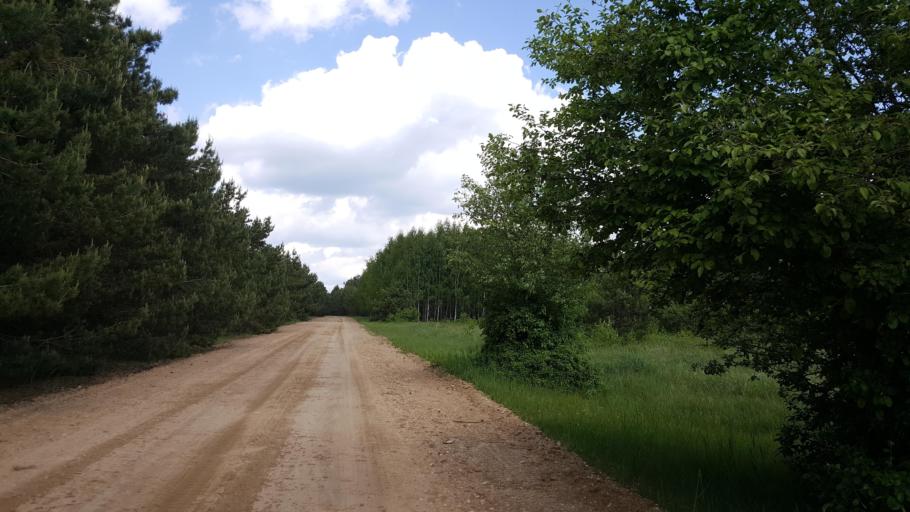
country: BY
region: Brest
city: Kamyanyets
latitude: 52.4831
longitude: 23.9656
